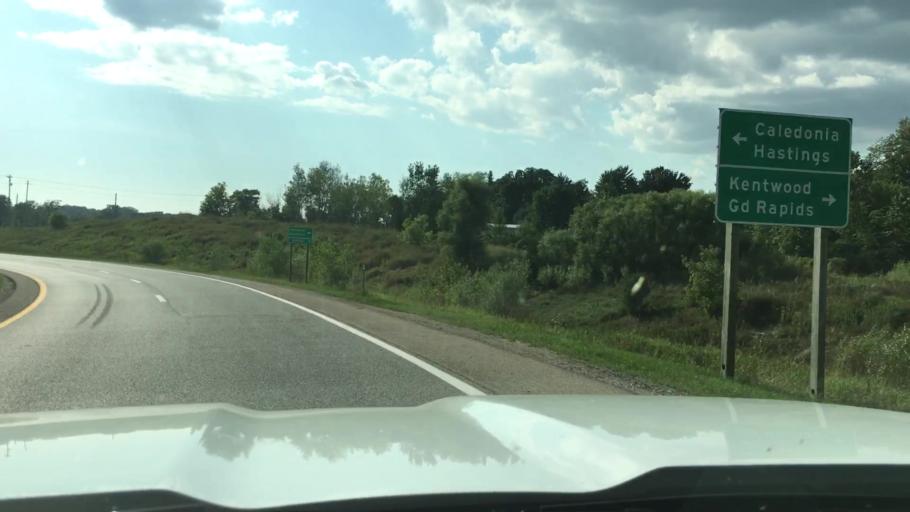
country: US
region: Michigan
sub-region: Kent County
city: Caledonia
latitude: 42.8534
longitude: -85.5377
